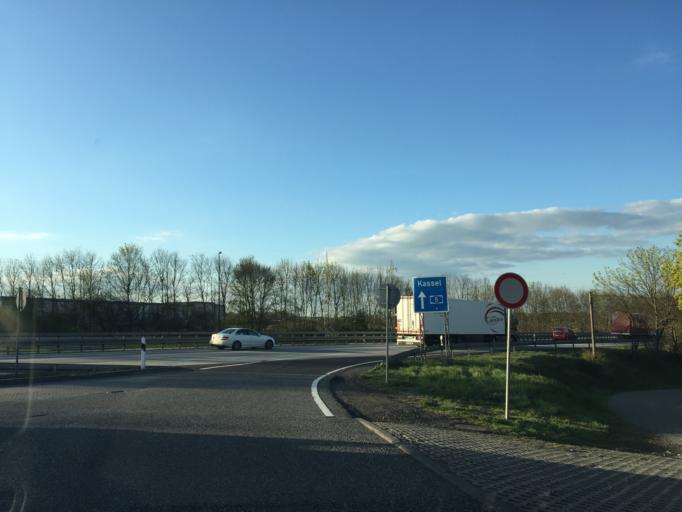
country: DE
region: Hesse
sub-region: Regierungsbezirk Giessen
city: Lich
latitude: 50.5212
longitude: 8.7577
